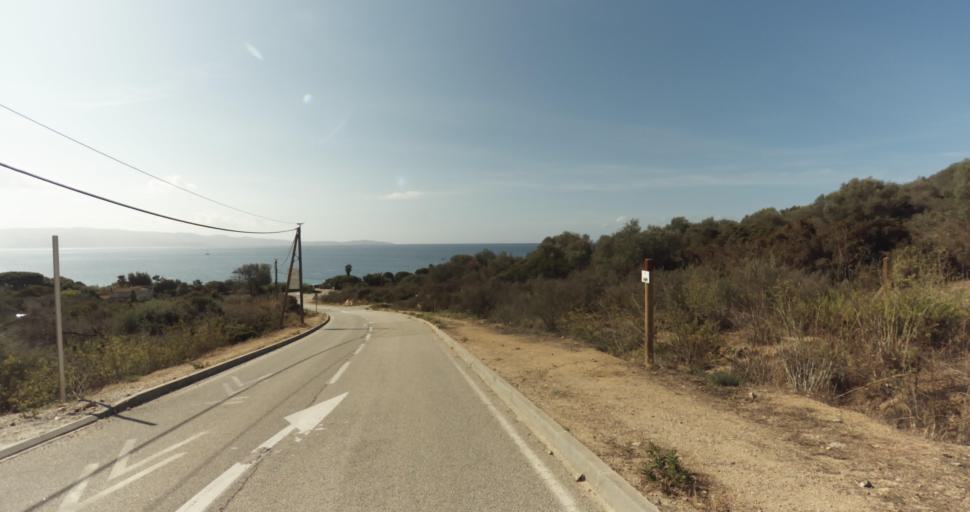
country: FR
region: Corsica
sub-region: Departement de la Corse-du-Sud
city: Ajaccio
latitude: 41.9129
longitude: 8.6437
